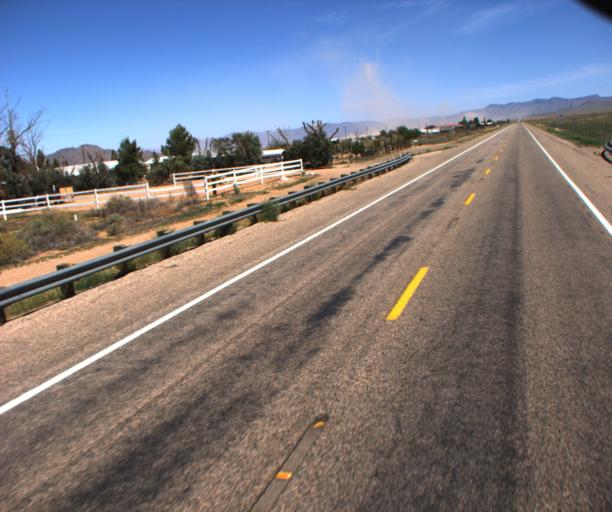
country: US
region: Arizona
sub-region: Mohave County
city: New Kingman-Butler
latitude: 35.2997
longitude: -113.9318
